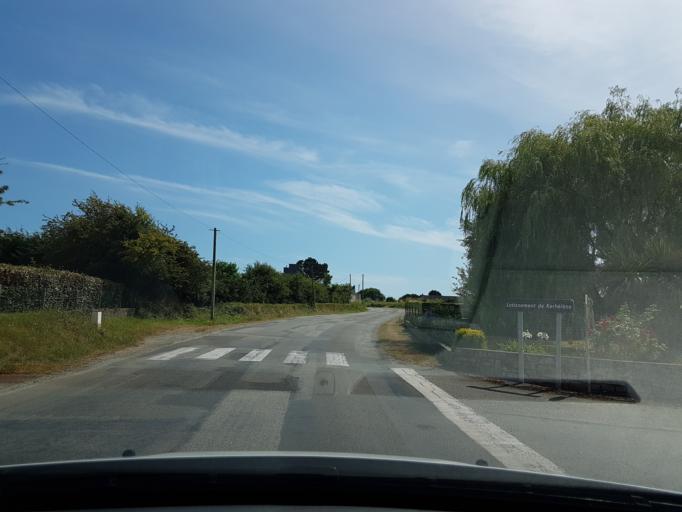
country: FR
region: Brittany
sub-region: Departement du Morbihan
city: Etel
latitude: 47.6737
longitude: -3.2206
